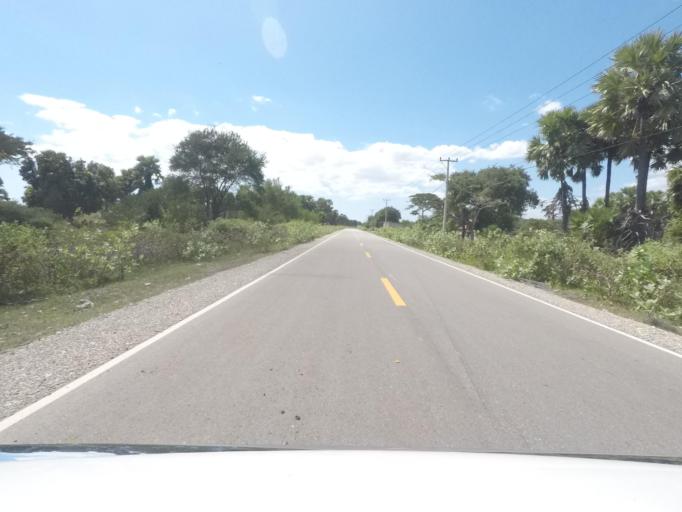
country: TL
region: Lautem
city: Lospalos
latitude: -8.3830
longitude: 126.8597
